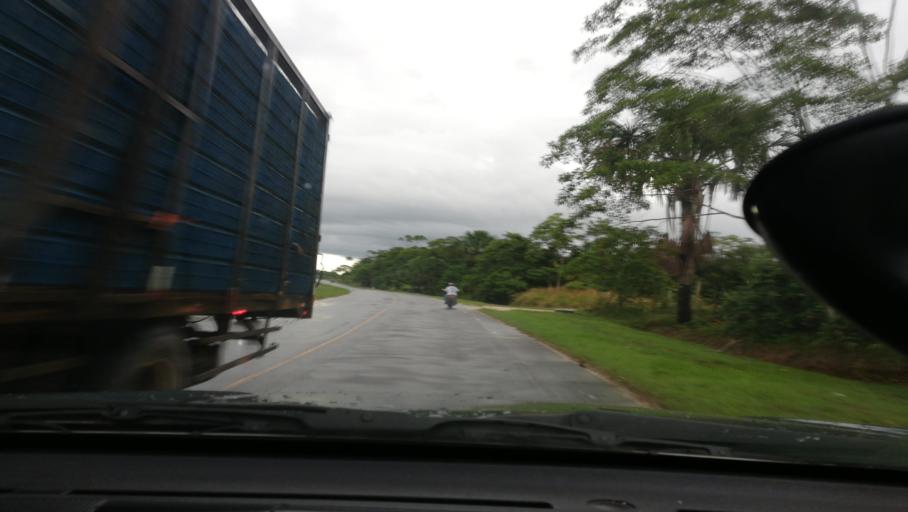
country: PE
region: Loreto
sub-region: Provincia de Maynas
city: Iquitos
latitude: -3.9120
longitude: -73.3634
